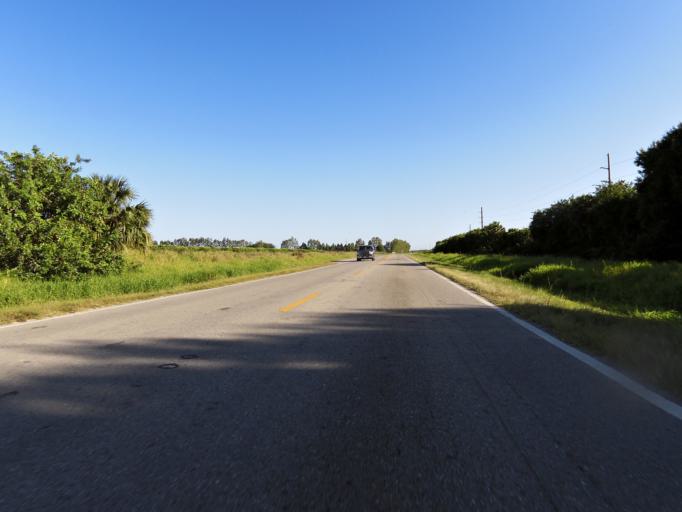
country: US
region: Florida
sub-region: Collier County
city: Immokalee
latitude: 26.3564
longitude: -81.4166
